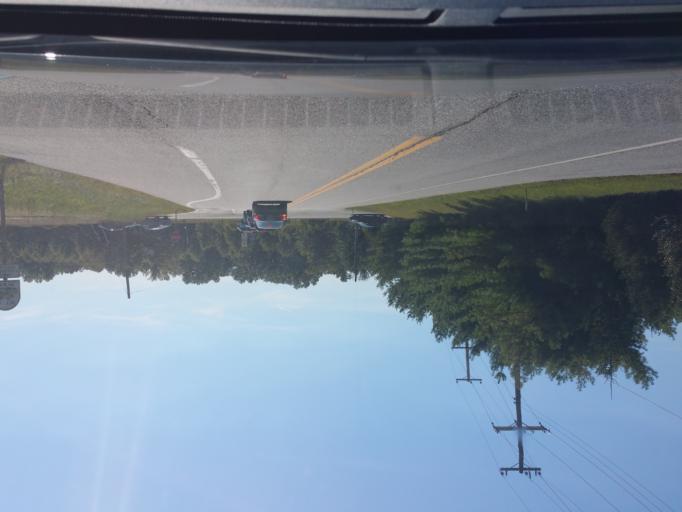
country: US
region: Maryland
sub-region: Harford County
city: Aberdeen
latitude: 39.5775
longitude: -76.1864
